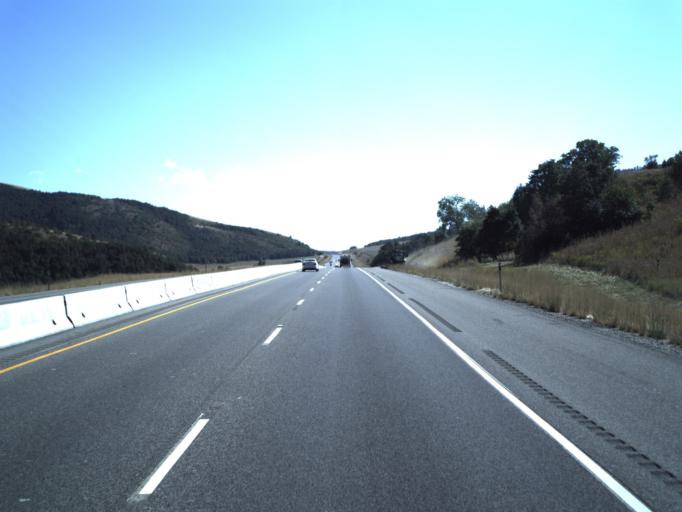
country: US
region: Utah
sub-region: Cache County
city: Wellsville
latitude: 41.5954
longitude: -111.9787
